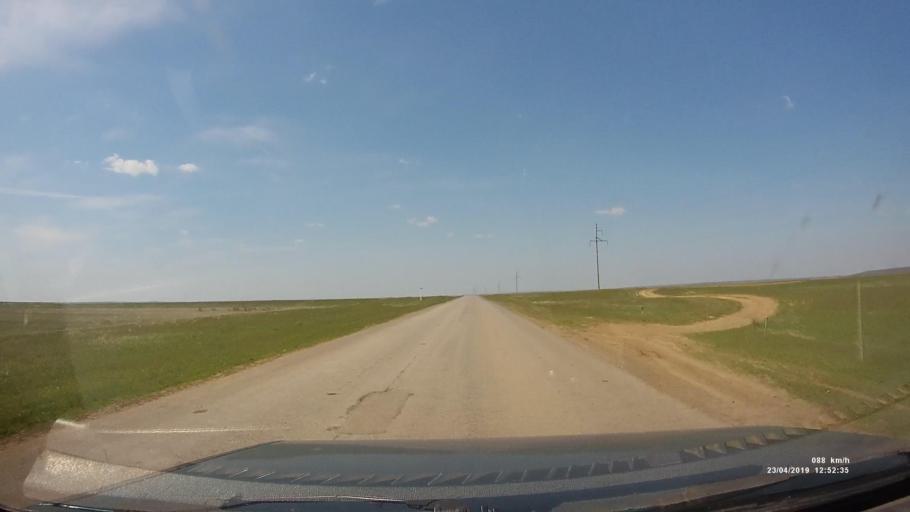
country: RU
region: Kalmykiya
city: Yashalta
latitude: 46.5660
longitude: 42.6076
